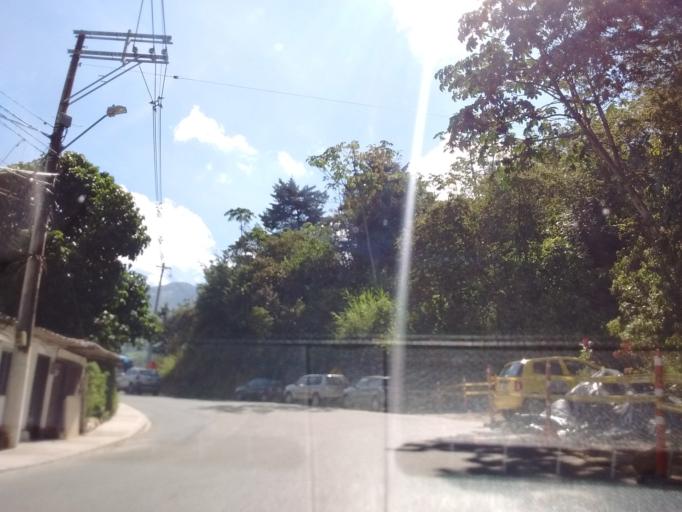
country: CO
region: Antioquia
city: Medellin
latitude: 6.2280
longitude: -75.5274
